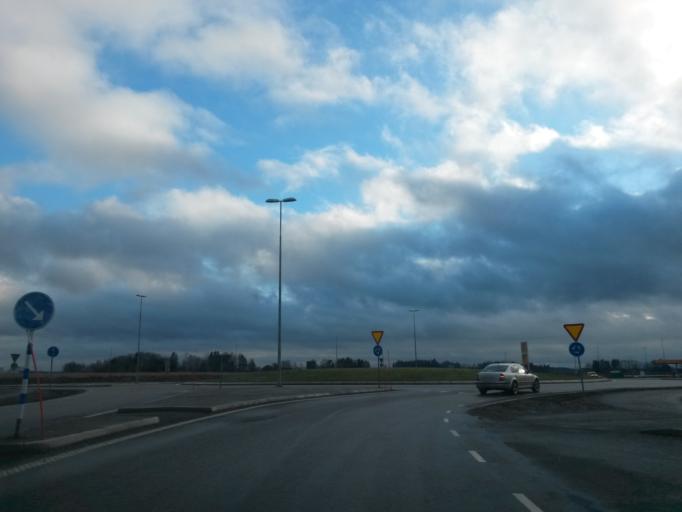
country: SE
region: Vaestra Goetaland
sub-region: Vara Kommun
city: Kvanum
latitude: 58.3296
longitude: 13.1325
